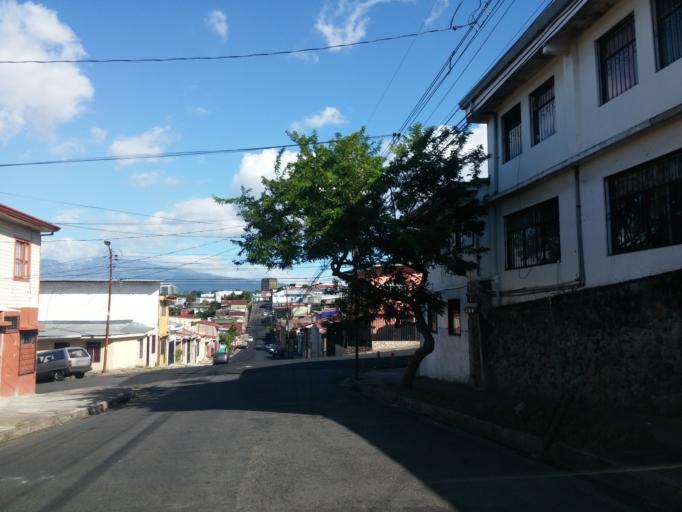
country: CR
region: San Jose
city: Colima
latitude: 9.9434
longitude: -84.0876
